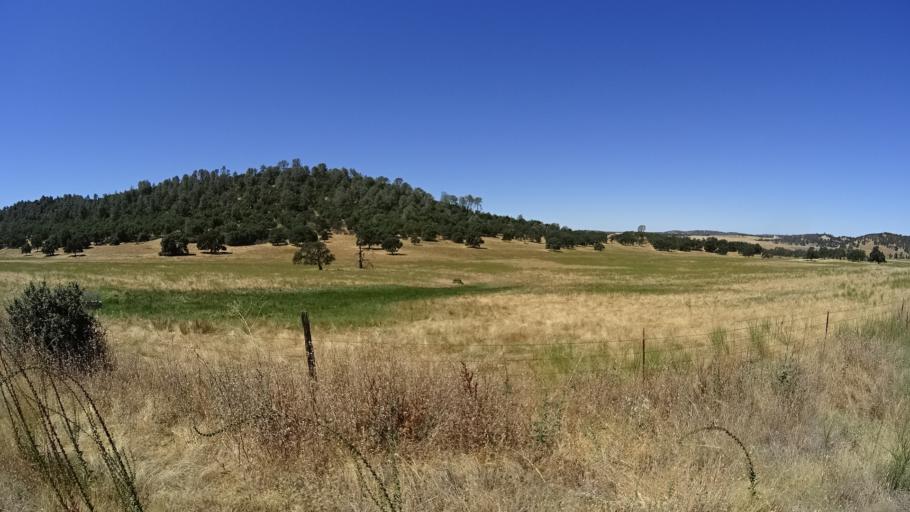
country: US
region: California
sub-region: Calaveras County
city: Copperopolis
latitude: 38.0050
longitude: -120.6641
